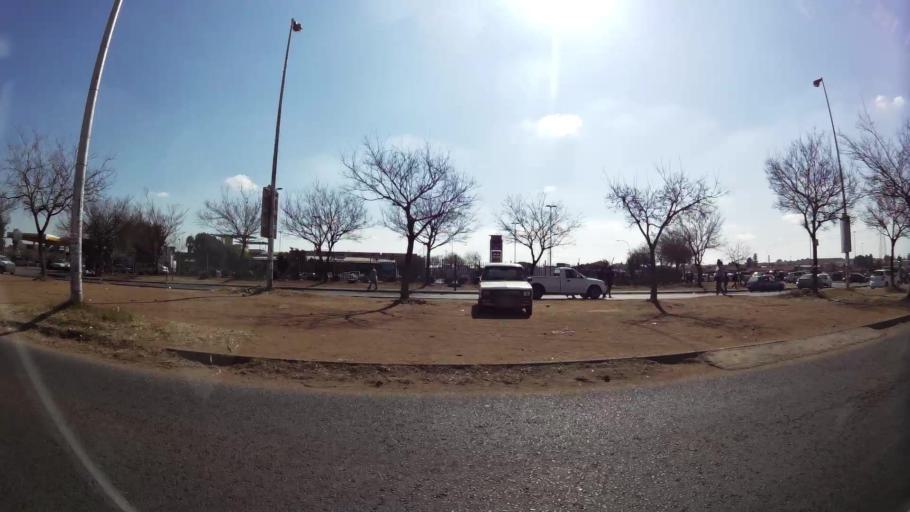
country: ZA
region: Gauteng
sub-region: City of Johannesburg Metropolitan Municipality
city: Soweto
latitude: -26.2870
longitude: 27.8502
